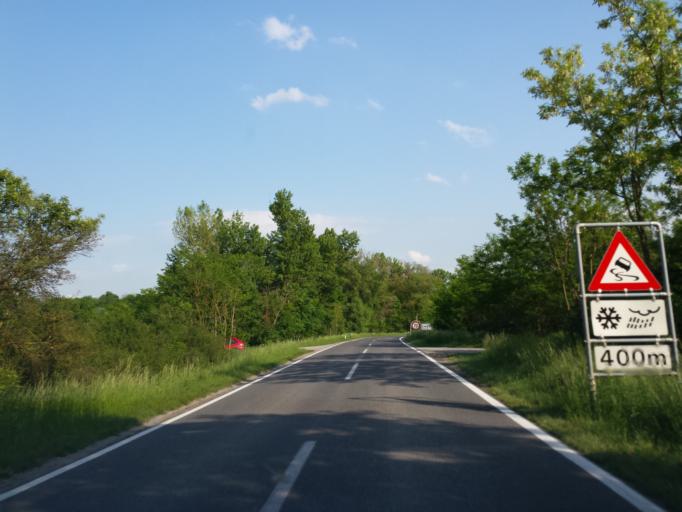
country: AT
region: Lower Austria
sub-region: Politischer Bezirk Ganserndorf
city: Marchegg
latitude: 48.2793
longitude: 16.8941
